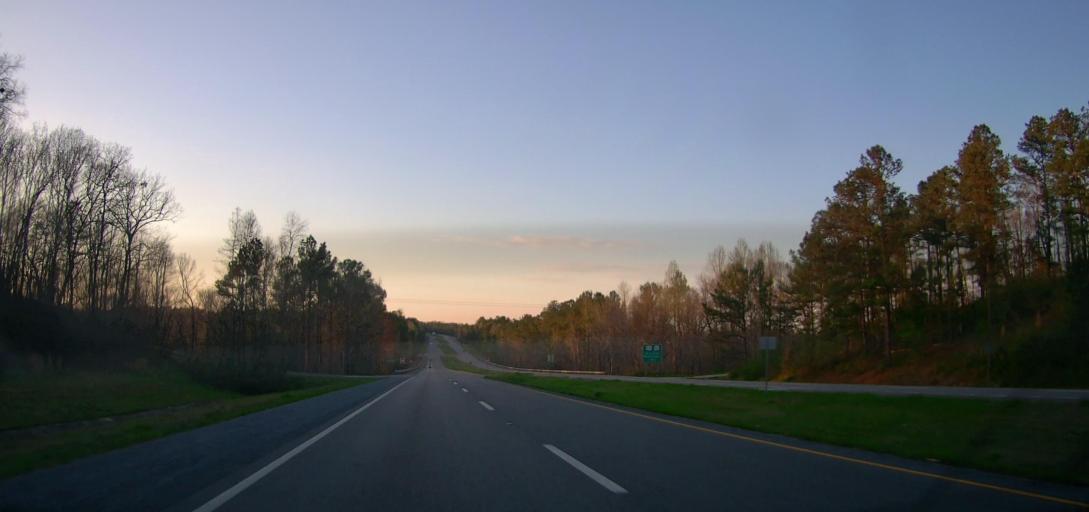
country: US
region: Alabama
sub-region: Talladega County
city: Sylacauga
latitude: 33.1285
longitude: -86.2448
